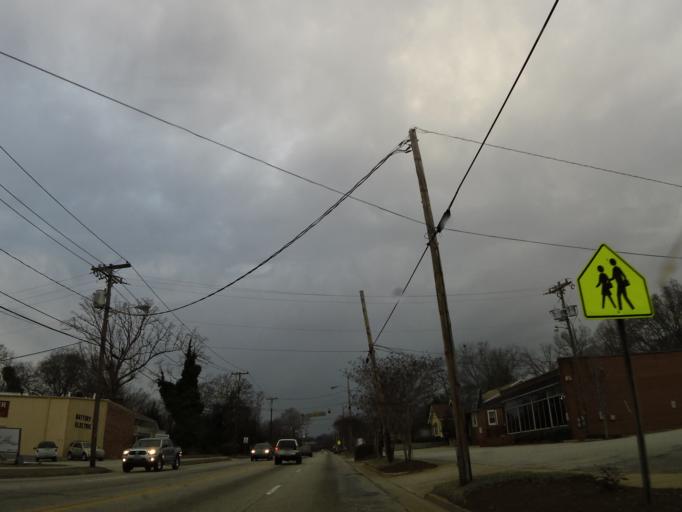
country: US
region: South Carolina
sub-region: Greenville County
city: Greenville
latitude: 34.8618
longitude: -82.3967
